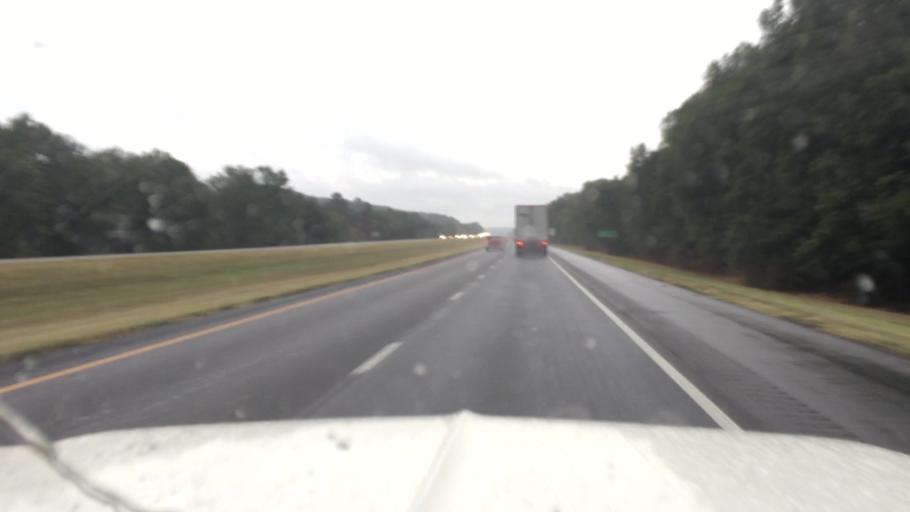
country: US
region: Alabama
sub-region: Morgan County
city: Falkville
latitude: 34.4015
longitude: -86.8977
